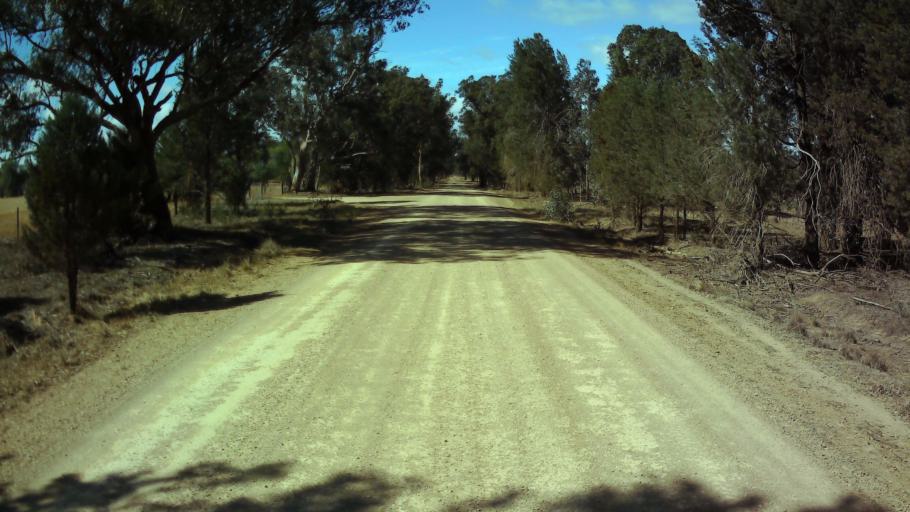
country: AU
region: New South Wales
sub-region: Weddin
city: Grenfell
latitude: -34.0416
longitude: 148.3156
